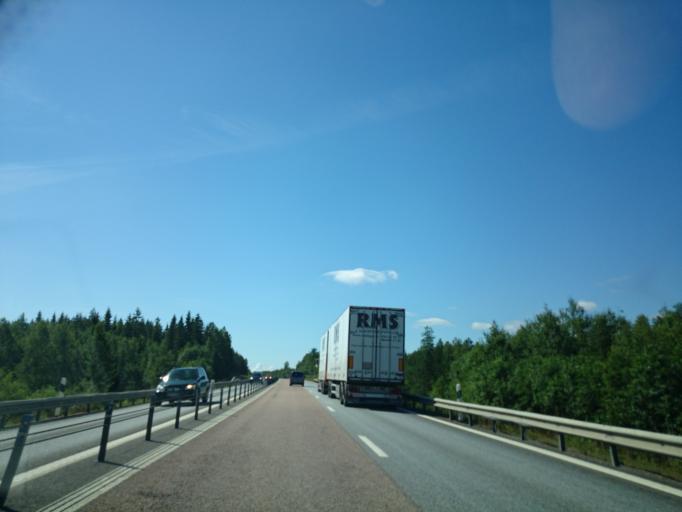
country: SE
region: Gaevleborg
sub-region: Gavle Kommun
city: Gavle
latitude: 60.8103
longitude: 17.0822
